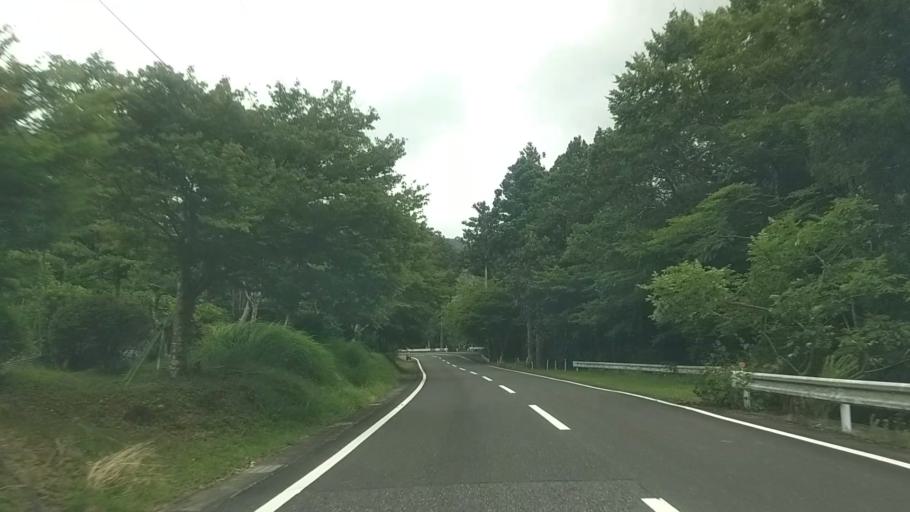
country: JP
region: Chiba
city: Kawaguchi
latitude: 35.1871
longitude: 140.1365
